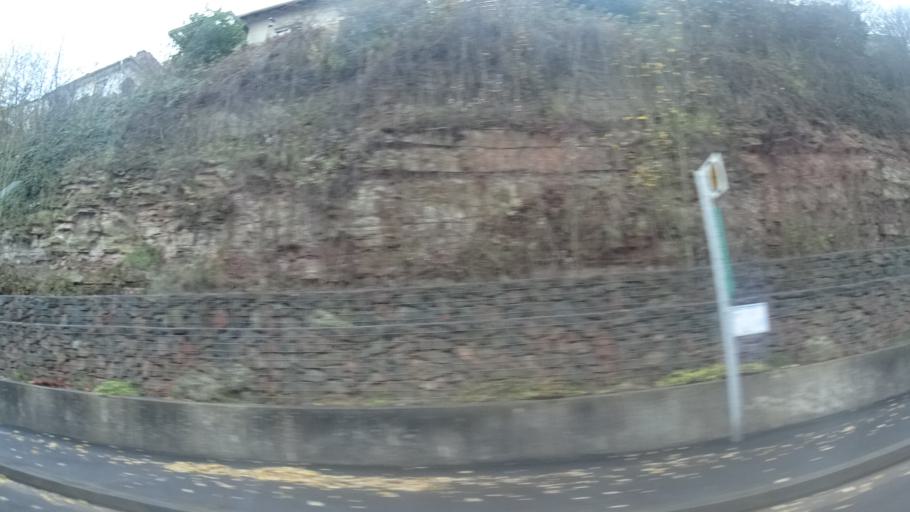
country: DE
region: Hesse
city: Heringen
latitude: 50.9083
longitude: 10.0142
